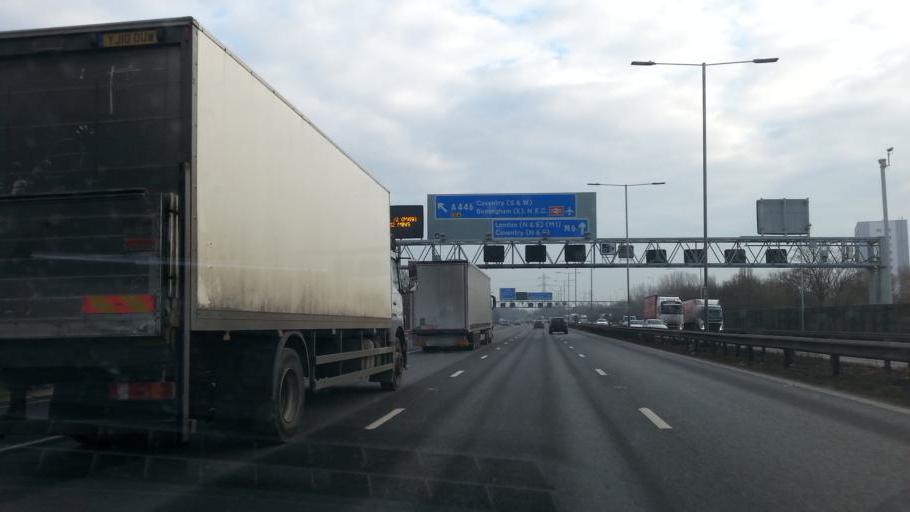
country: GB
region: England
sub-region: Solihull
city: Chelmsley Wood
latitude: 52.4857
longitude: -1.7260
